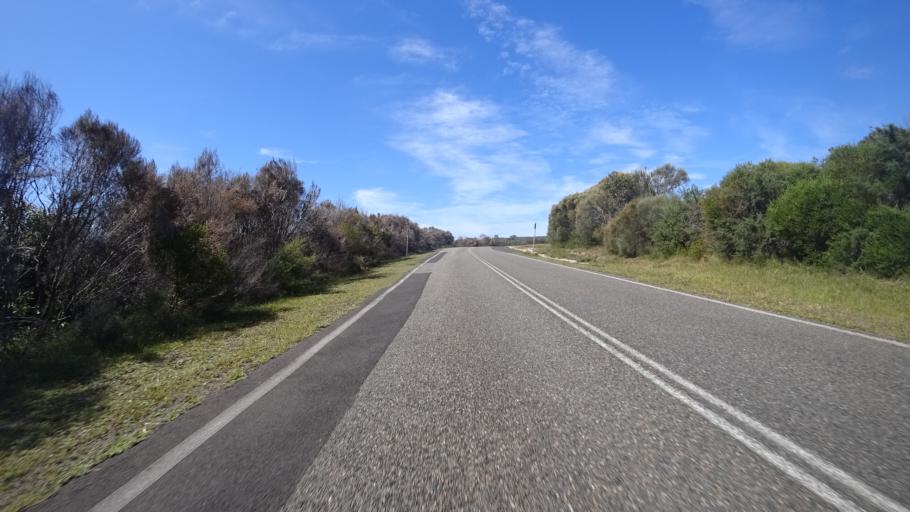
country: AU
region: New South Wales
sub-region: Shoalhaven Shire
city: Falls Creek
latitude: -35.1448
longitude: 150.7069
